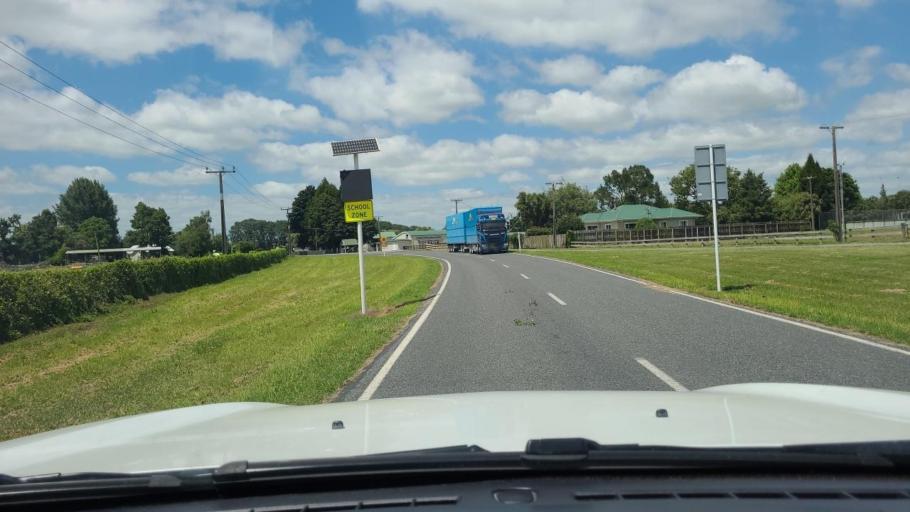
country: NZ
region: Waikato
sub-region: Matamata-Piako District
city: Matamata
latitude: -37.8786
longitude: 175.7585
